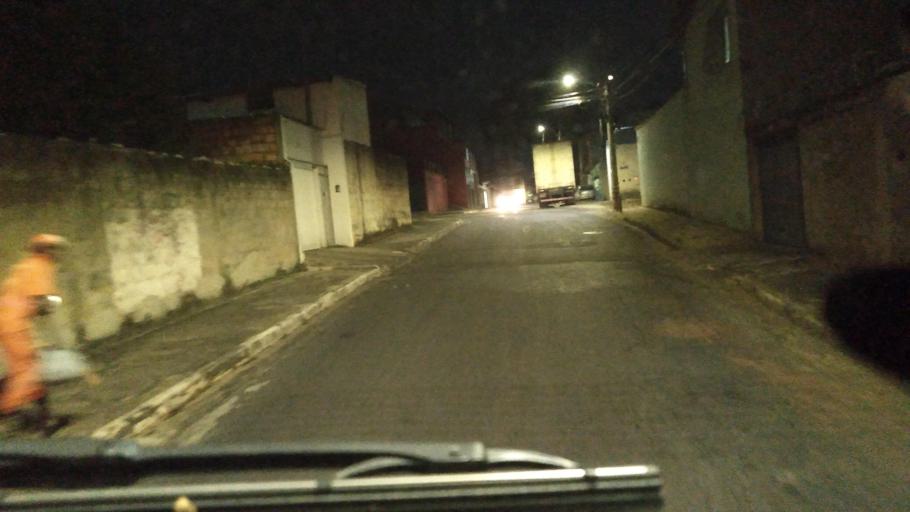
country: BR
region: Minas Gerais
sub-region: Belo Horizonte
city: Belo Horizonte
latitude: -19.8853
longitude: -43.9557
